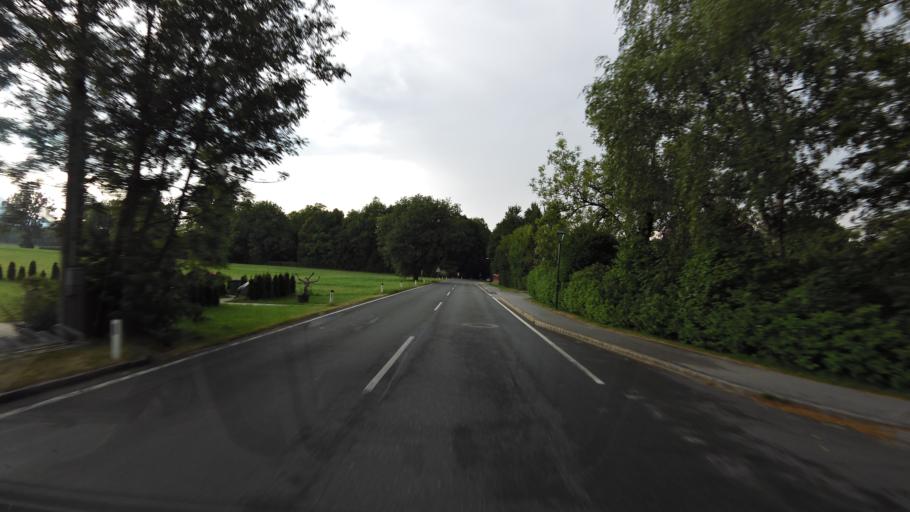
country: AT
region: Salzburg
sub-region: Politischer Bezirk Salzburg-Umgebung
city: Anif
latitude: 47.7593
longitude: 13.0609
